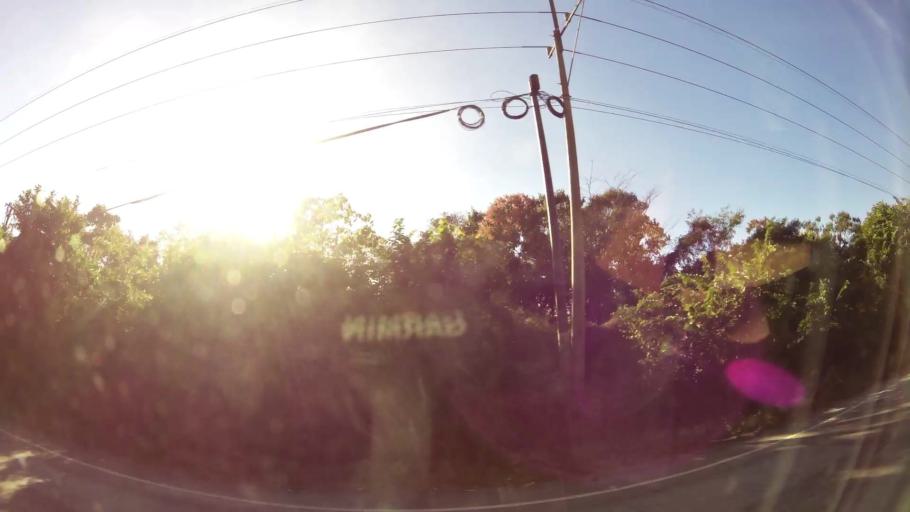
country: SV
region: Santa Ana
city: Metapan
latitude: 14.2637
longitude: -89.4597
